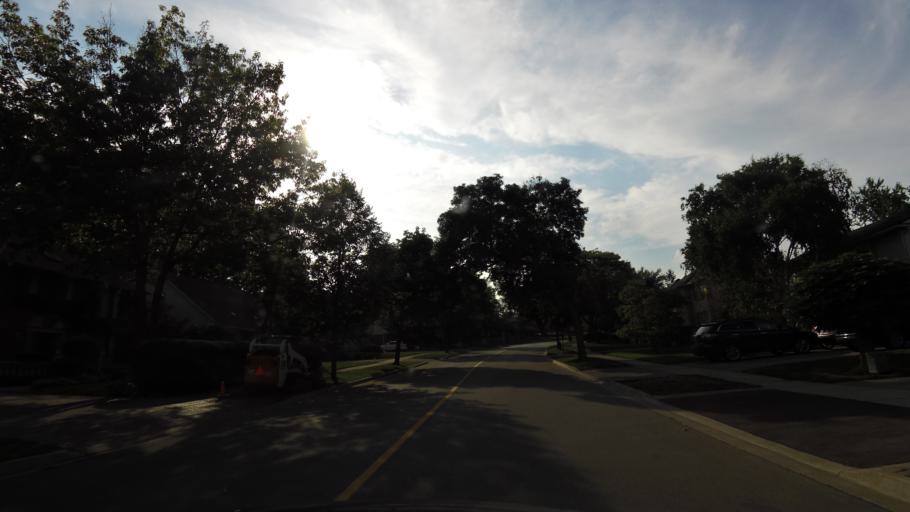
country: CA
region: Ontario
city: Burlington
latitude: 43.3447
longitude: -79.8449
